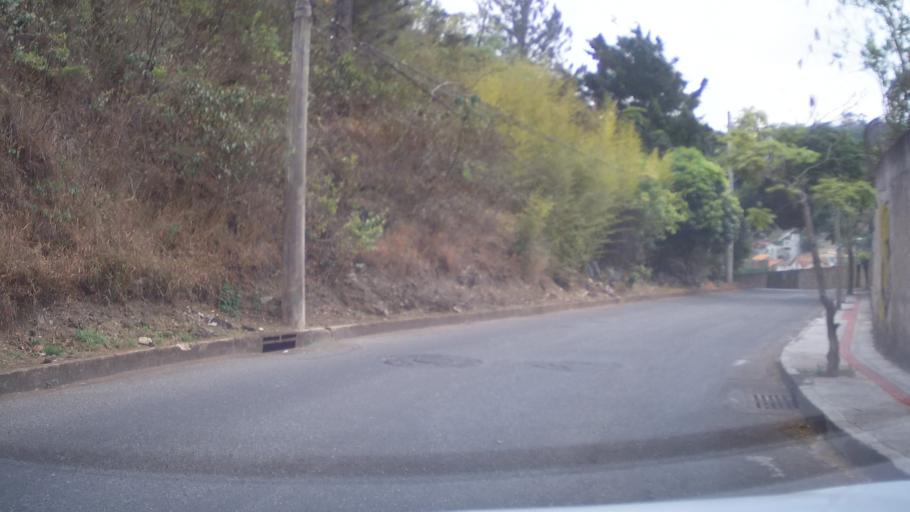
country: BR
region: Minas Gerais
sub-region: Belo Horizonte
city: Belo Horizonte
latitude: -19.9556
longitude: -43.9173
